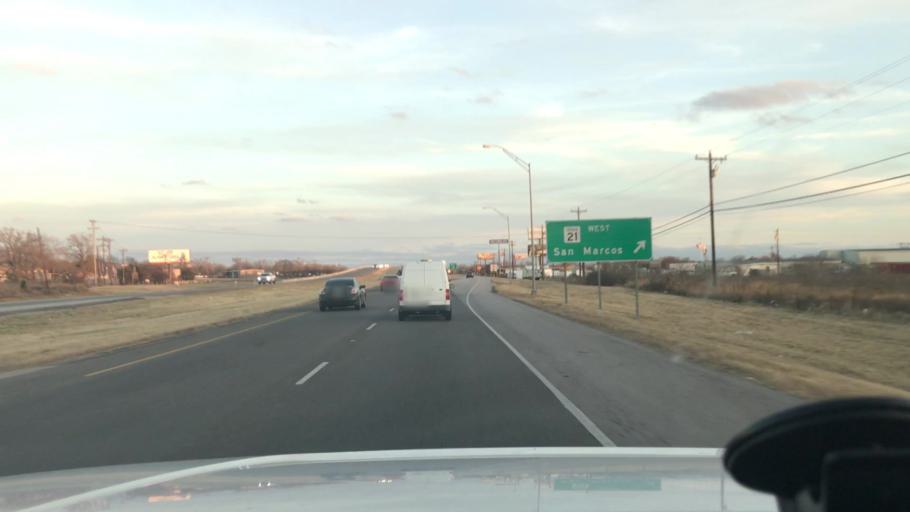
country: US
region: Texas
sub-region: Bastrop County
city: Wyldwood
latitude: 30.1155
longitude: -97.4212
